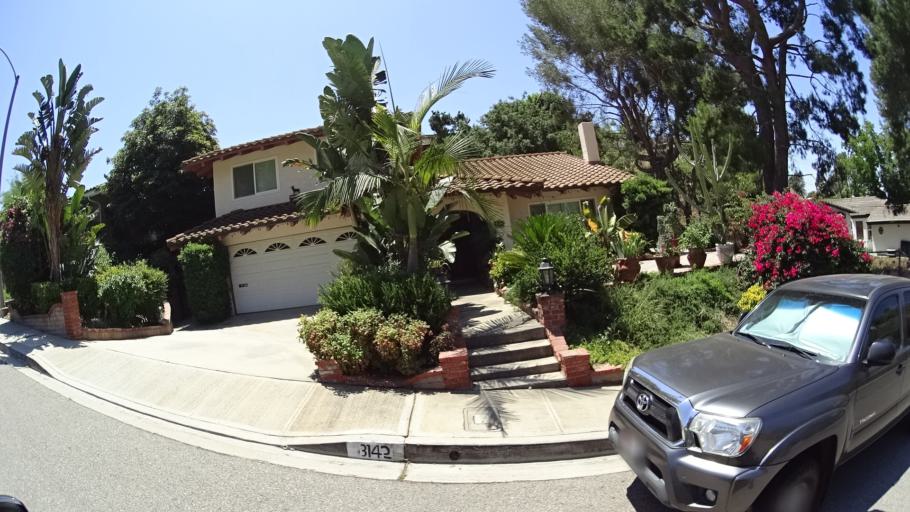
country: US
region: California
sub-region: Los Angeles County
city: Burbank
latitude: 34.2144
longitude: -118.3298
